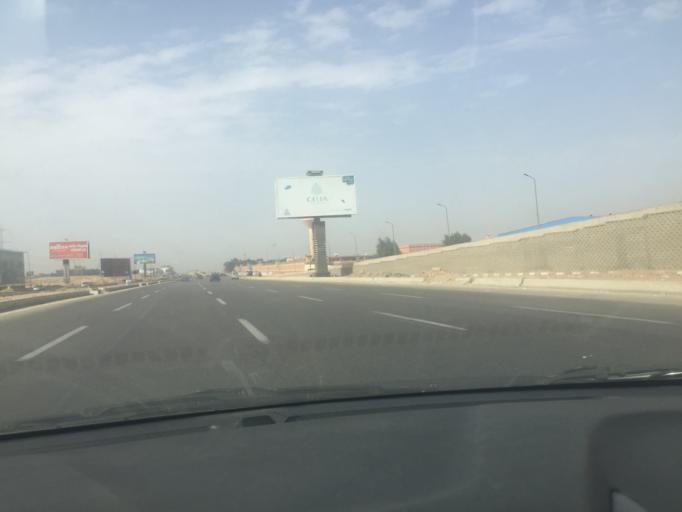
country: EG
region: Muhafazat al Qalyubiyah
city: Al Khankah
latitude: 30.0831
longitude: 31.4695
